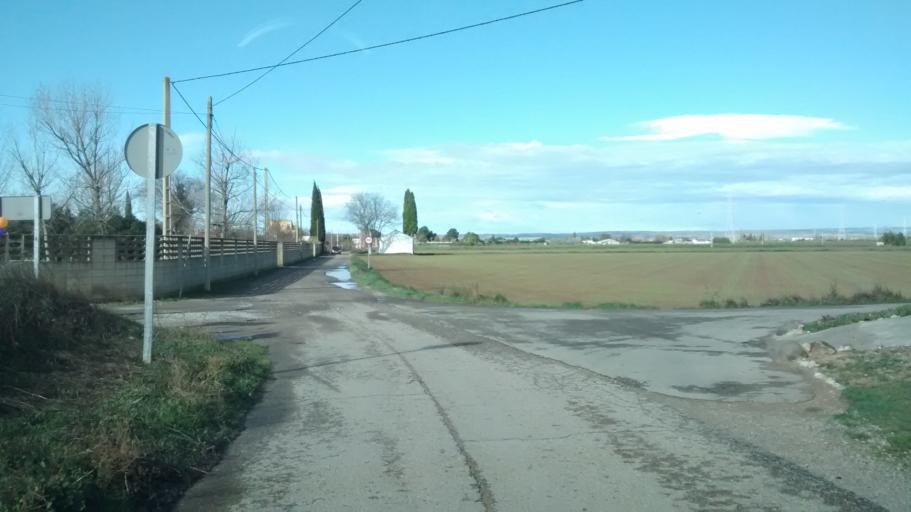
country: ES
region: Aragon
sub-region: Provincia de Zaragoza
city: Villanueva de Gallego
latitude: 41.7293
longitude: -0.7867
